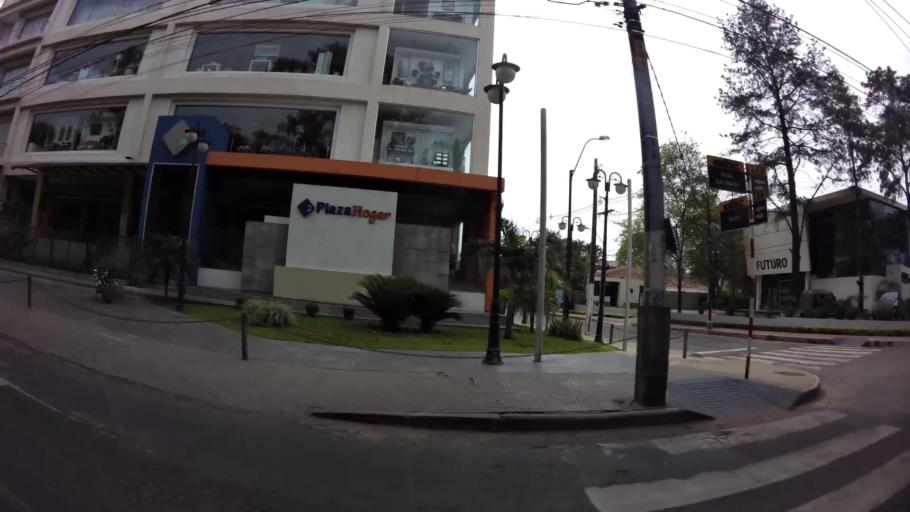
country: PY
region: Asuncion
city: Asuncion
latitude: -25.2909
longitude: -57.5745
